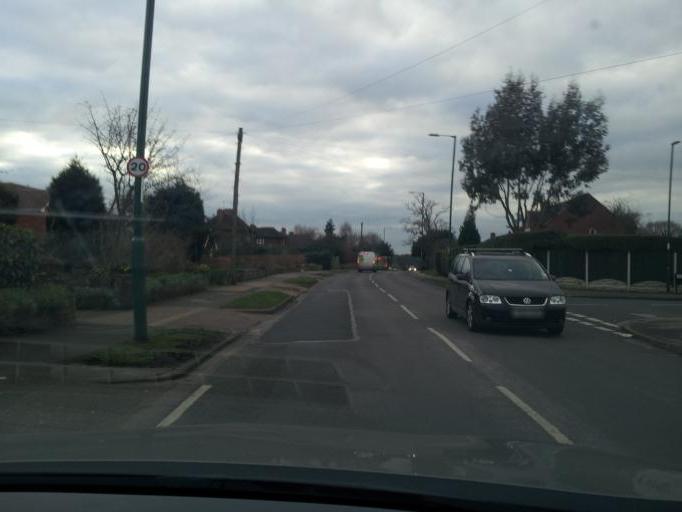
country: GB
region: England
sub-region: Nottinghamshire
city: Kimberley
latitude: 52.9512
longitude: -1.2243
